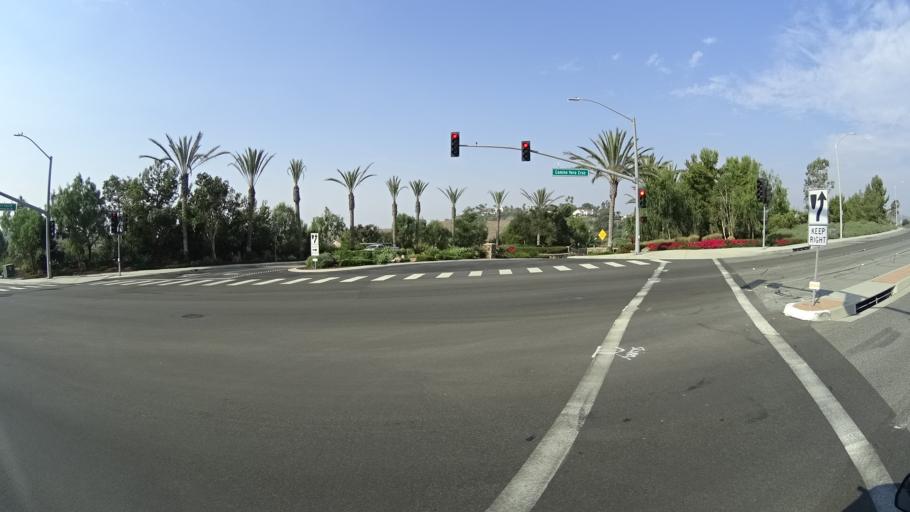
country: US
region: California
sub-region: Orange County
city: San Clemente
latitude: 33.4605
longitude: -117.6187
